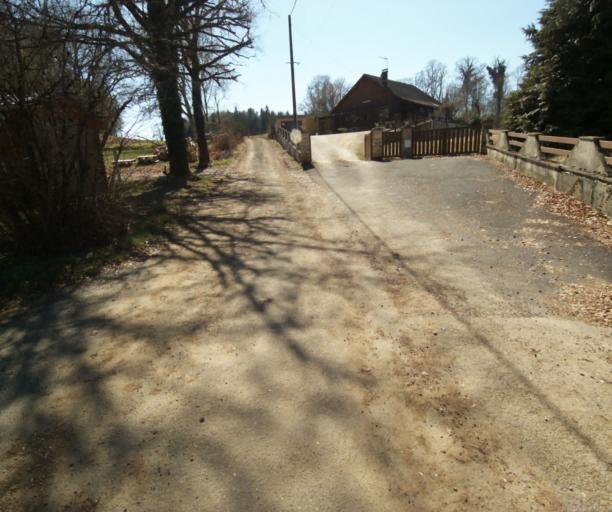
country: FR
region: Limousin
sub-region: Departement de la Correze
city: Saint-Clement
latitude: 45.3140
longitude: 1.7052
